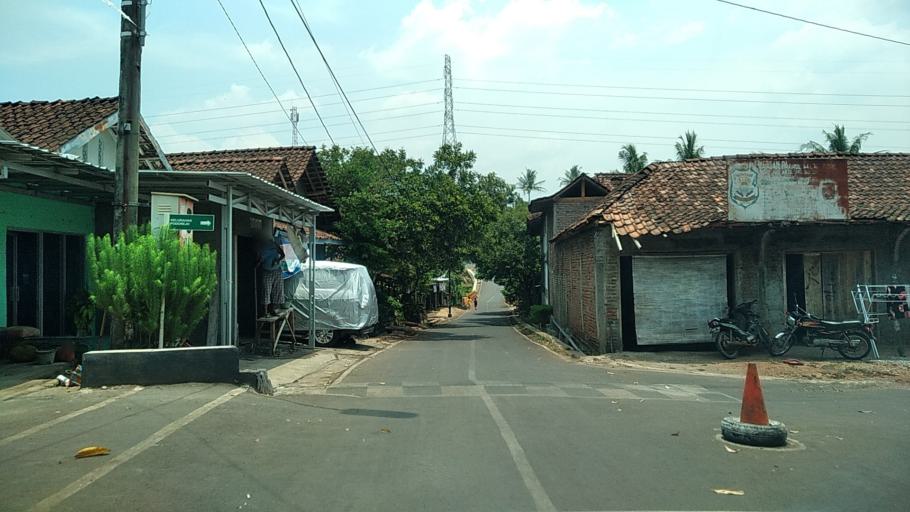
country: ID
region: Central Java
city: Semarang
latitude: -7.0085
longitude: 110.2935
